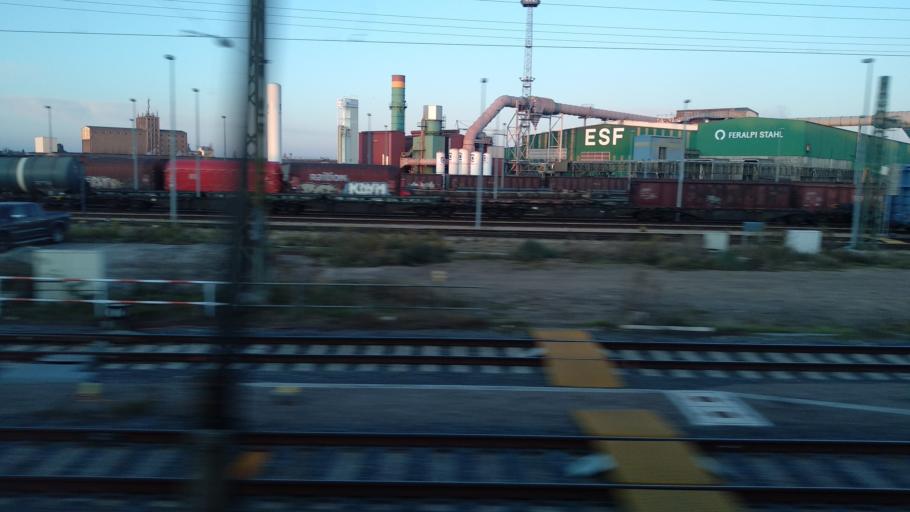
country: DE
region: Saxony
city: Riesa
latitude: 51.3109
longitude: 13.2728
